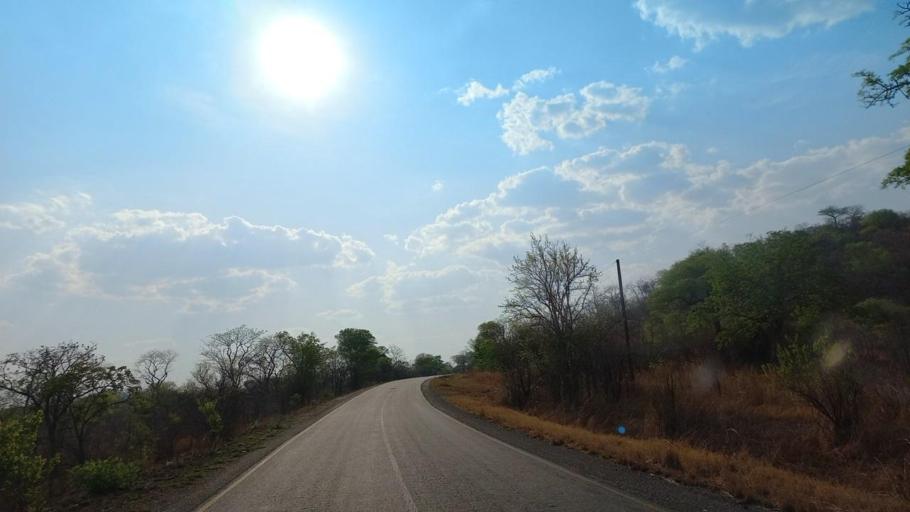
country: ZM
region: Lusaka
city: Luangwa
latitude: -14.9837
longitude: 30.1582
